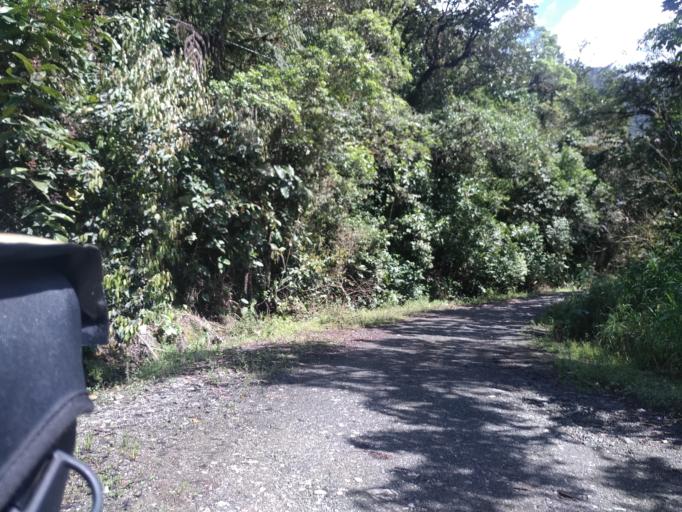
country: EC
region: Tungurahua
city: Banos
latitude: -1.4037
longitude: -78.2806
